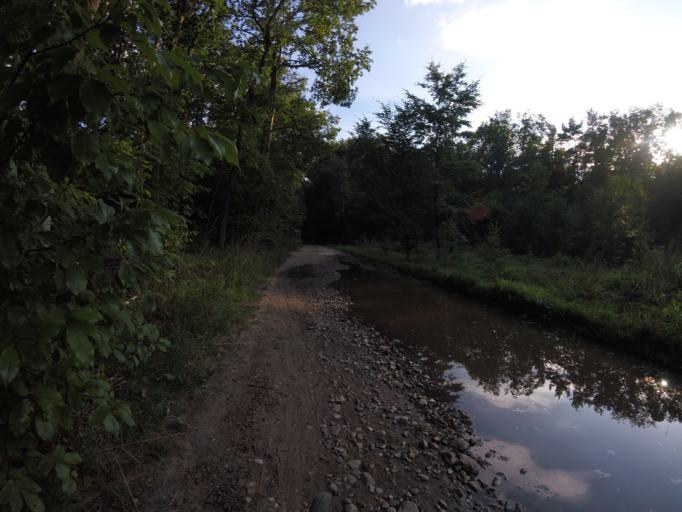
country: DE
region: Brandenburg
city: Petershagen
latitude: 52.5658
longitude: 13.8220
